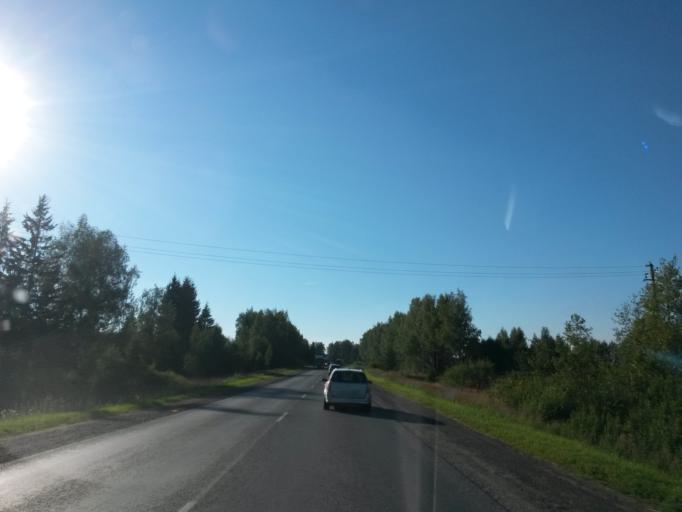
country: RU
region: Ivanovo
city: Novo-Talitsy
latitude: 57.0240
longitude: 40.7644
